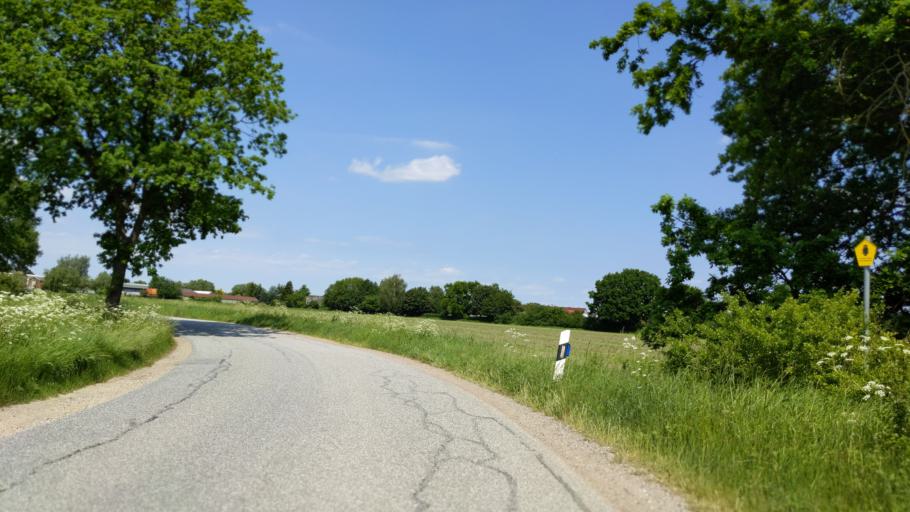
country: DE
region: Schleswig-Holstein
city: Krummesse
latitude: 53.8265
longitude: 10.6624
